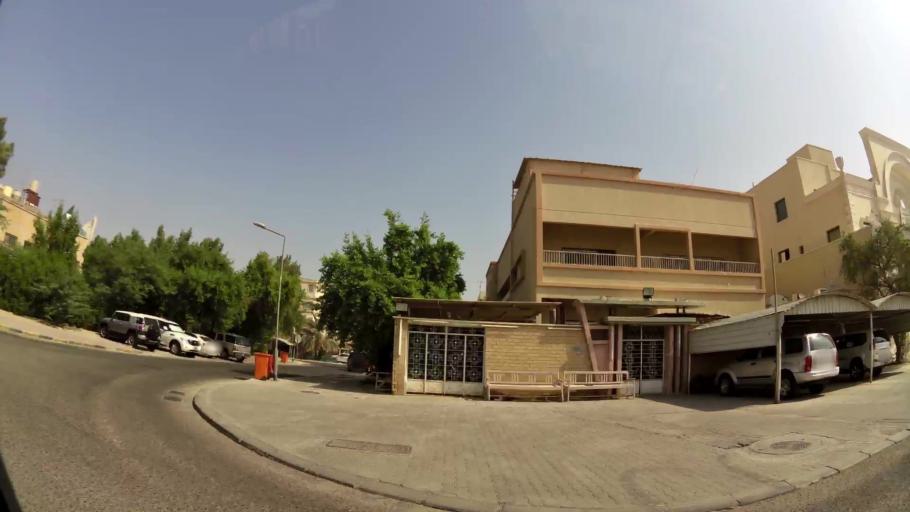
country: KW
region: Al Asimah
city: Ad Dasmah
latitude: 29.3611
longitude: 47.9931
